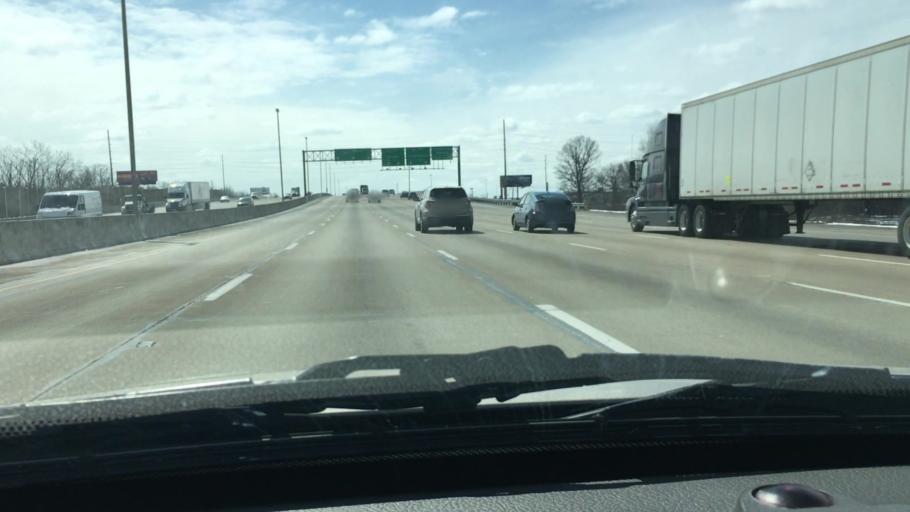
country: US
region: Indiana
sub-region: Marion County
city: Lawrence
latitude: 39.8132
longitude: -86.0311
